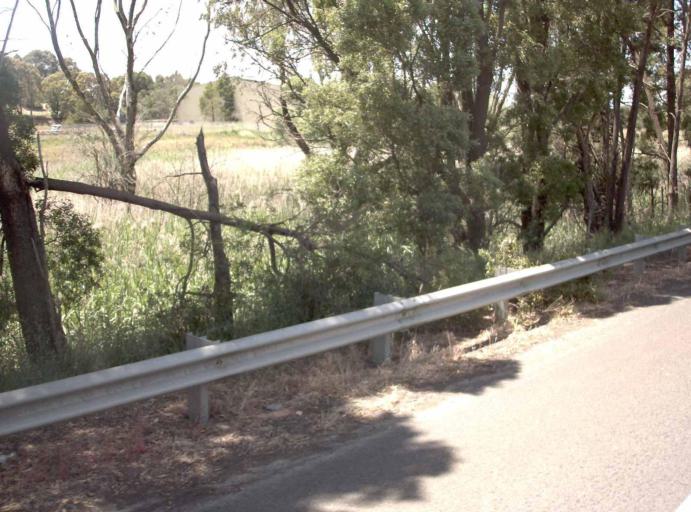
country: AU
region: Victoria
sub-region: Baw Baw
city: Warragul
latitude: -38.1702
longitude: 145.9211
